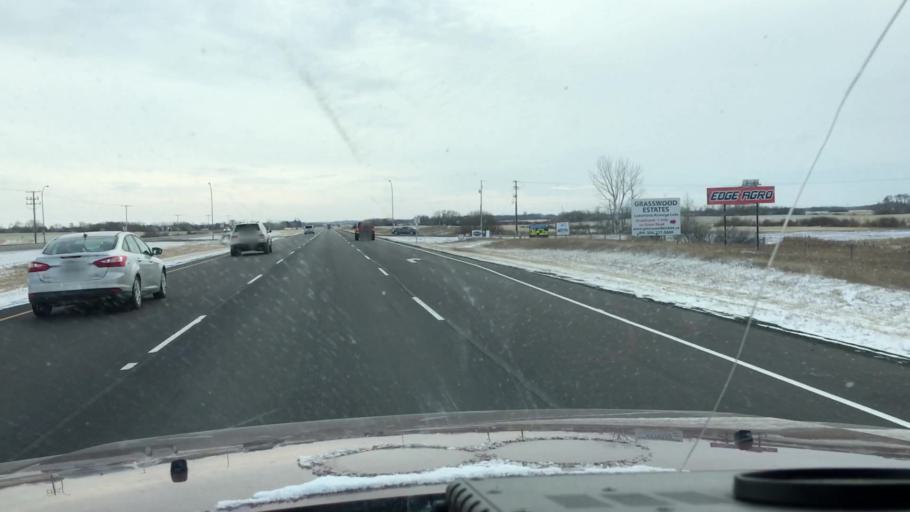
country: CA
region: Saskatchewan
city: Saskatoon
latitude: 52.0285
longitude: -106.5829
